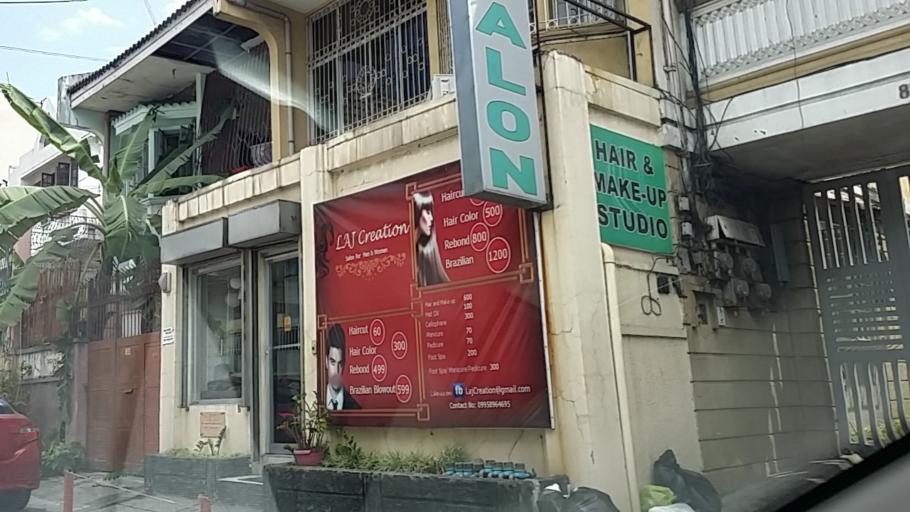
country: PH
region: Metro Manila
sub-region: Mandaluyong
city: Mandaluyong City
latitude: 14.5803
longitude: 121.0511
